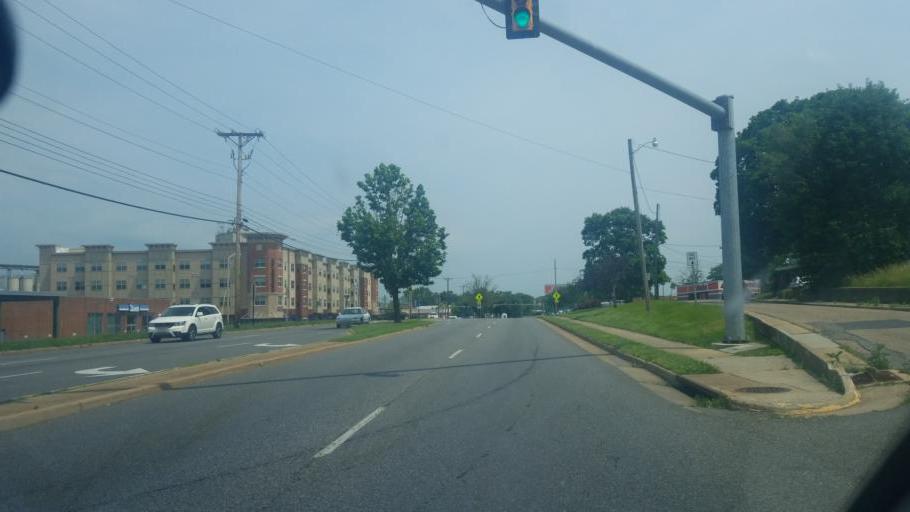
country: US
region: Virginia
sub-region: City of Harrisonburg
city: Harrisonburg
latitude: 38.4511
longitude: -78.8660
